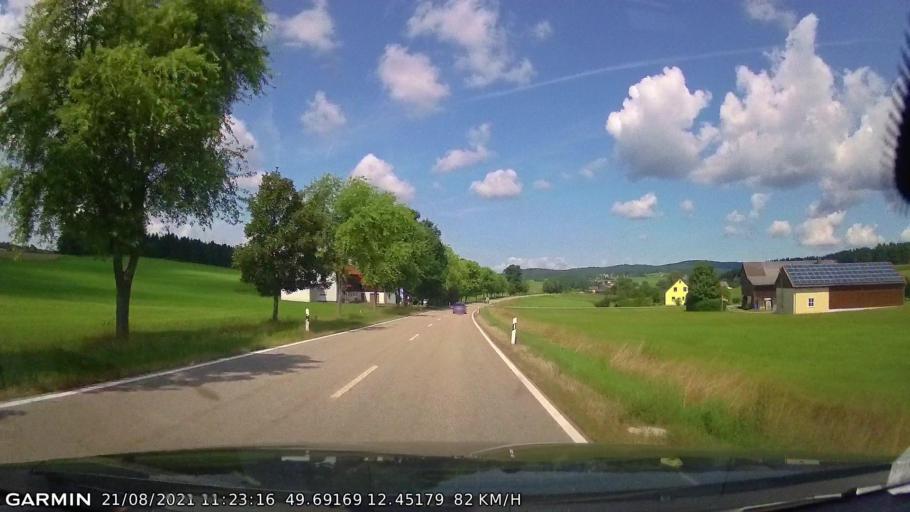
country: DE
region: Bavaria
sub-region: Upper Palatinate
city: Georgenberg
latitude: 49.6916
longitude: 12.4519
